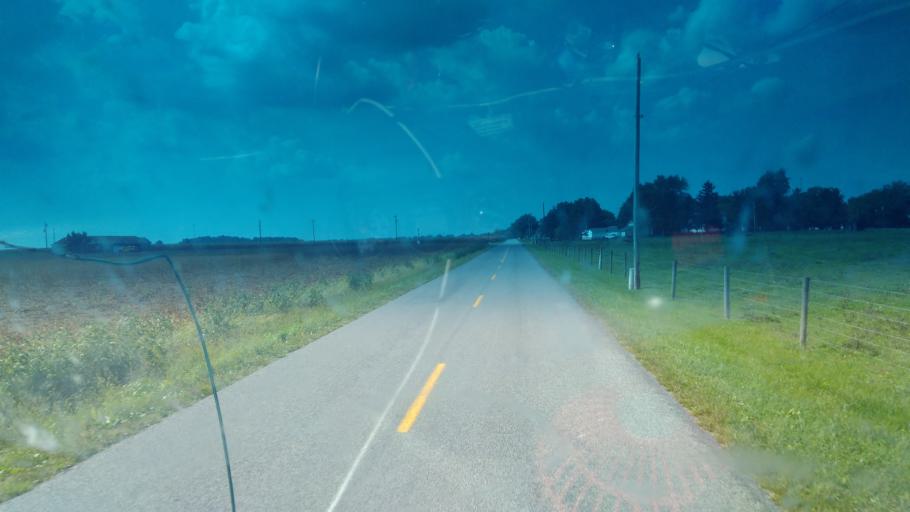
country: US
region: Ohio
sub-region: Hardin County
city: Ada
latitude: 40.7028
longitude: -83.9158
